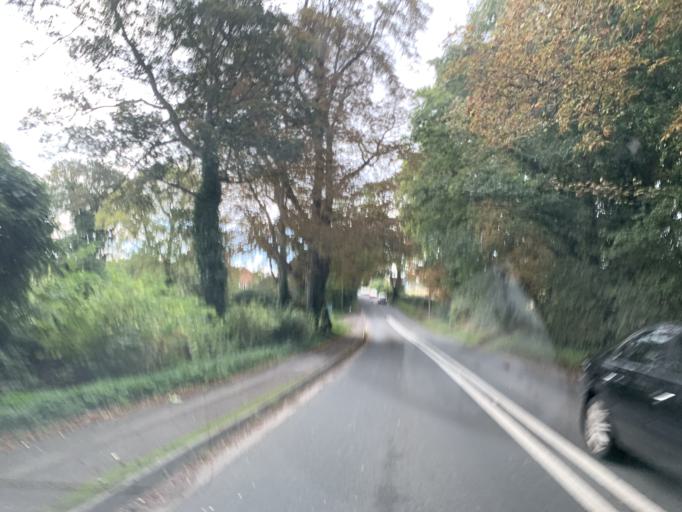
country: GB
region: England
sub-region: Wiltshire
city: Shrewton
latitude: 51.1884
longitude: -1.8964
